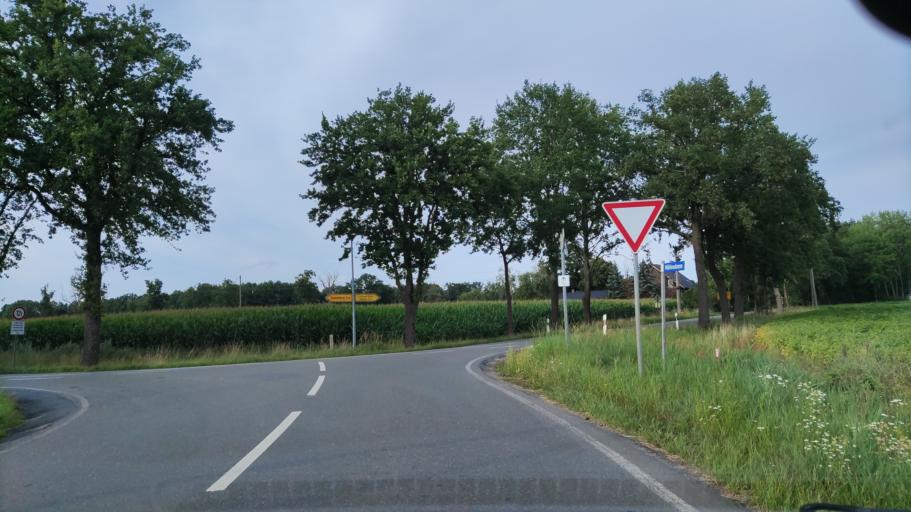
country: DE
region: Lower Saxony
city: Jameln
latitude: 53.0537
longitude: 11.1377
